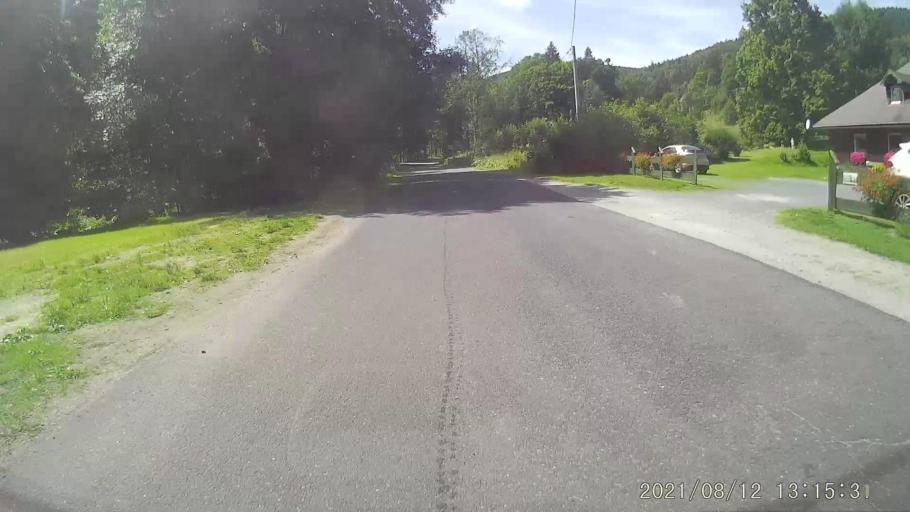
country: PL
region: Lower Silesian Voivodeship
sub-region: Powiat klodzki
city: Stronie Slaskie
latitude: 50.2614
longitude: 16.8689
